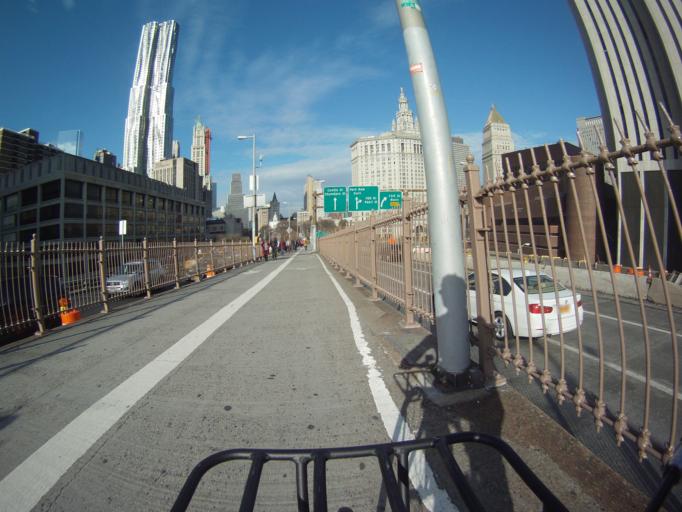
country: US
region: New York
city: New York City
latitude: 40.7101
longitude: -74.0018
